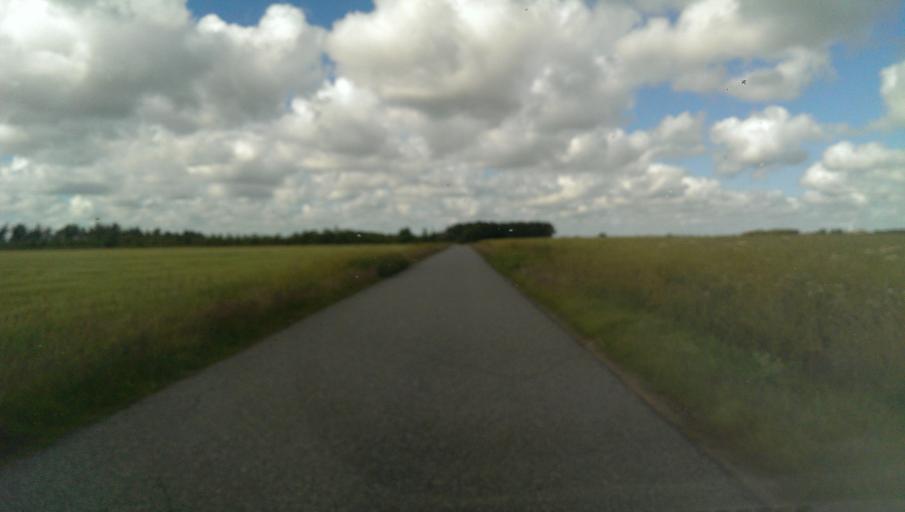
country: DK
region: Central Jutland
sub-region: Holstebro Kommune
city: Ulfborg
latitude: 56.2684
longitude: 8.2462
